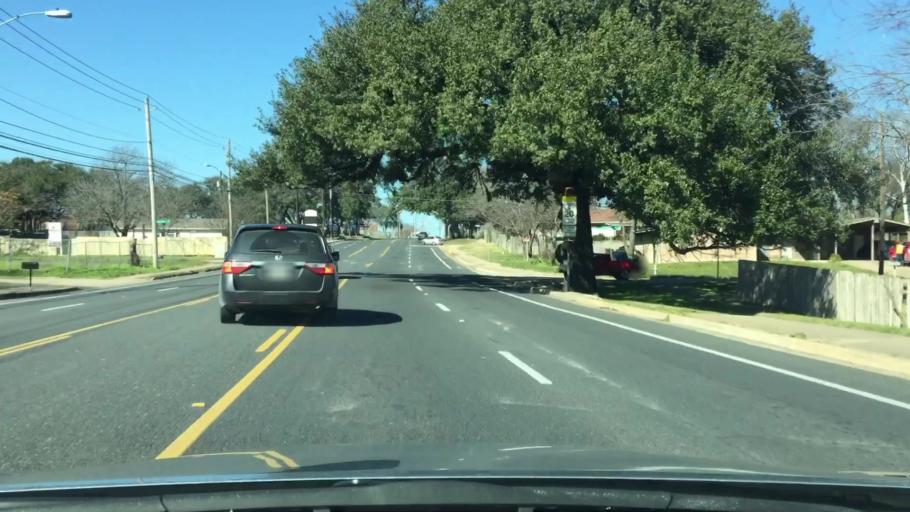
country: US
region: Texas
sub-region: Travis County
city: Wells Branch
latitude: 30.3787
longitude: -97.6806
